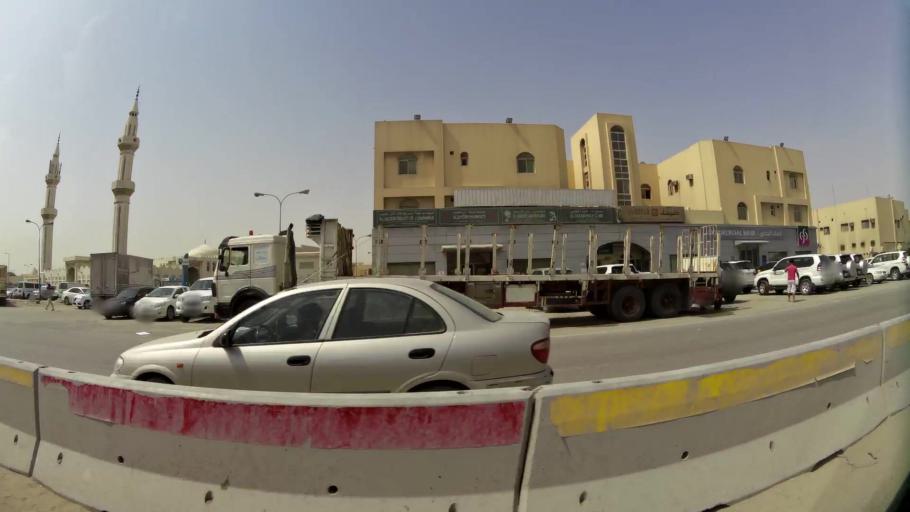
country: QA
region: Baladiyat ar Rayyan
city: Ar Rayyan
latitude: 25.1956
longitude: 51.4314
